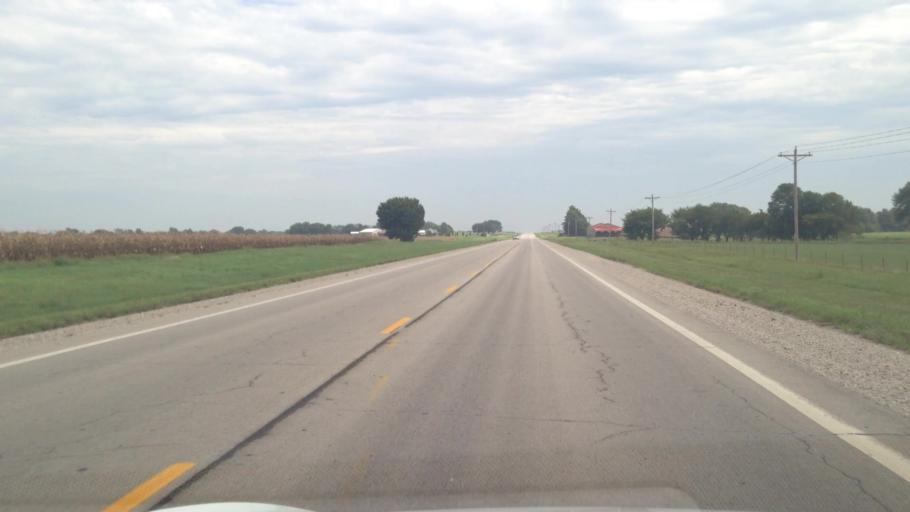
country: US
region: Kansas
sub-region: Crawford County
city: Girard
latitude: 37.5144
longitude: -94.9409
